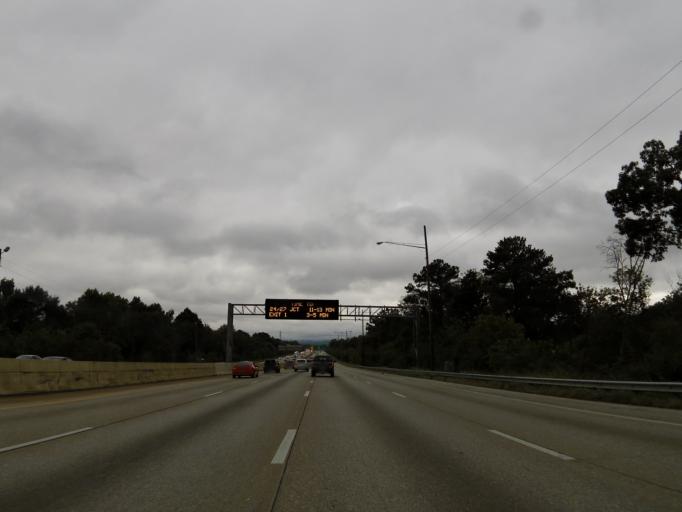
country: US
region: Tennessee
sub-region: Hamilton County
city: East Brainerd
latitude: 35.0108
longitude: -85.1912
